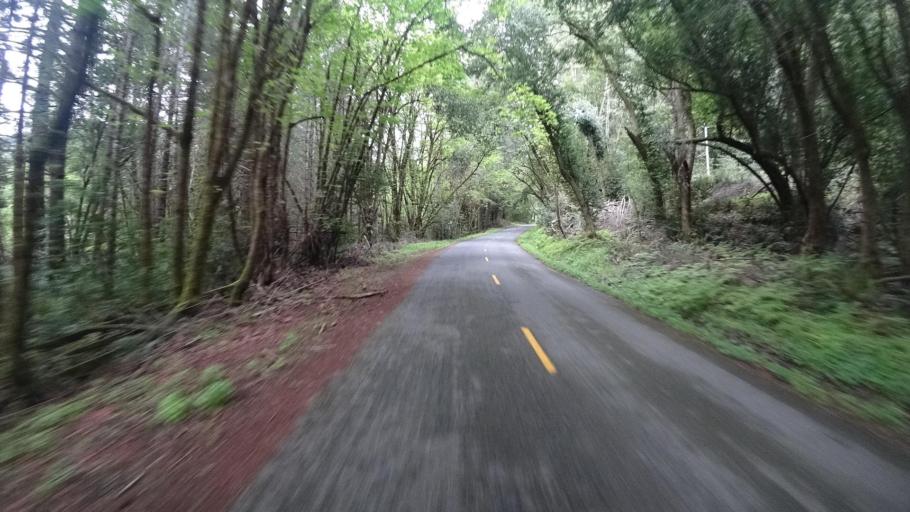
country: US
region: California
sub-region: Humboldt County
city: Blue Lake
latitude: 40.9606
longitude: -123.8383
